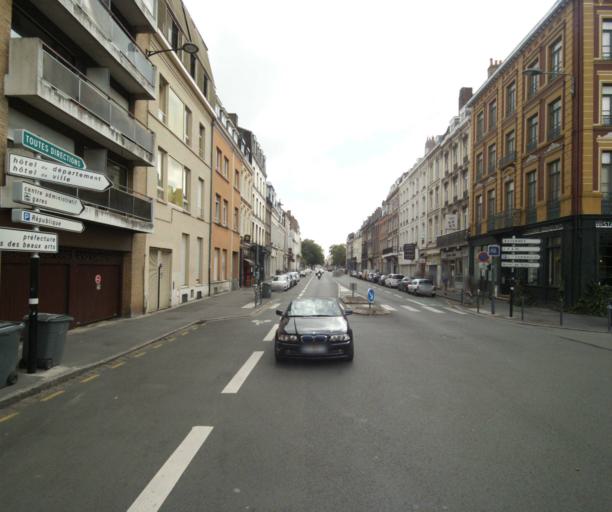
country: FR
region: Nord-Pas-de-Calais
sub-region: Departement du Nord
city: Lille
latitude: 50.6291
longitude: 3.0589
